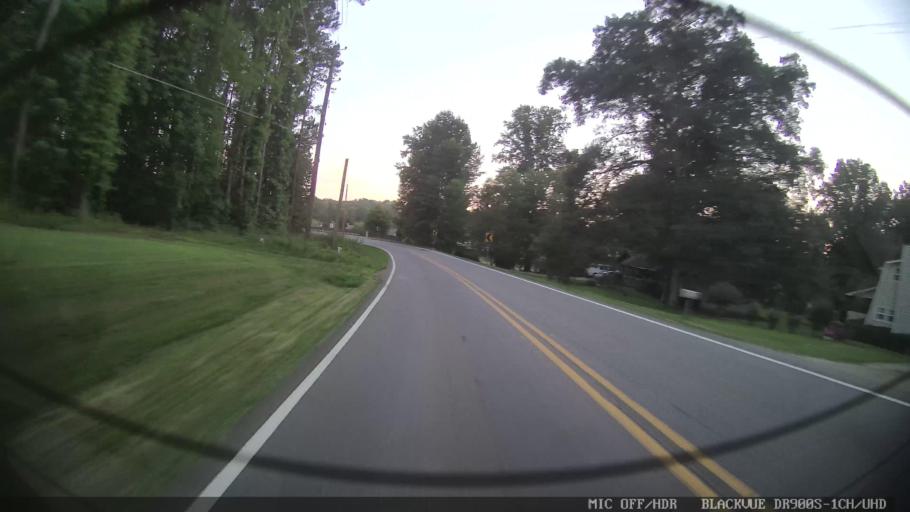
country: US
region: Georgia
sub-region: Forsyth County
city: Cumming
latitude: 34.2896
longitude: -84.1690
